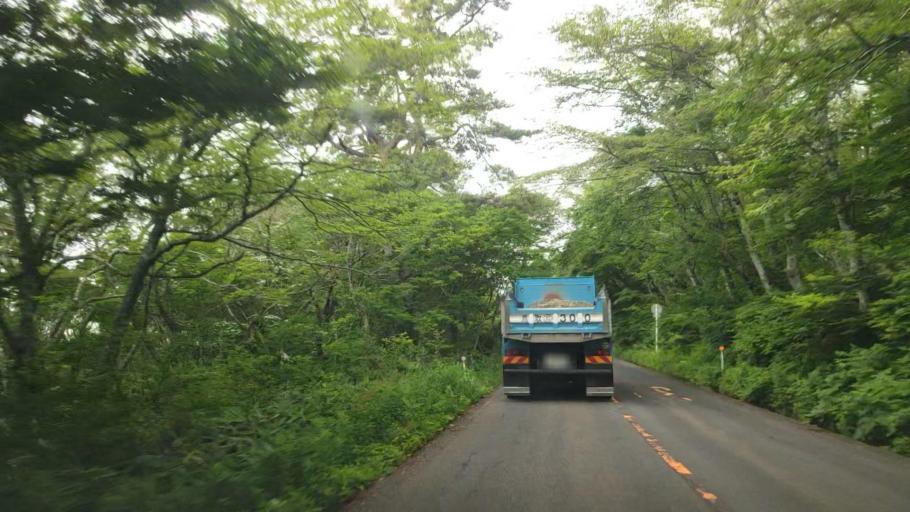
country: JP
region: Tottori
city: Yonago
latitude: 35.3733
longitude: 133.5176
